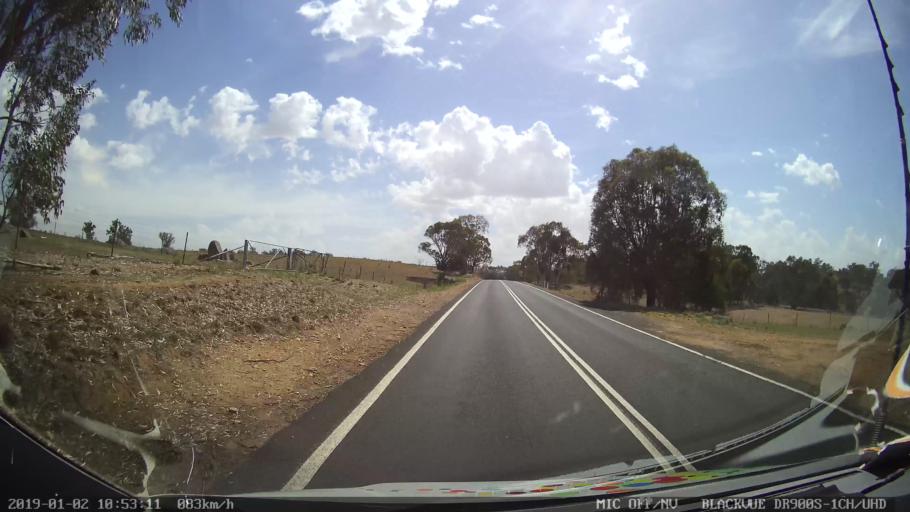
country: AU
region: New South Wales
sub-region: Cootamundra
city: Cootamundra
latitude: -34.6802
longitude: 148.2731
